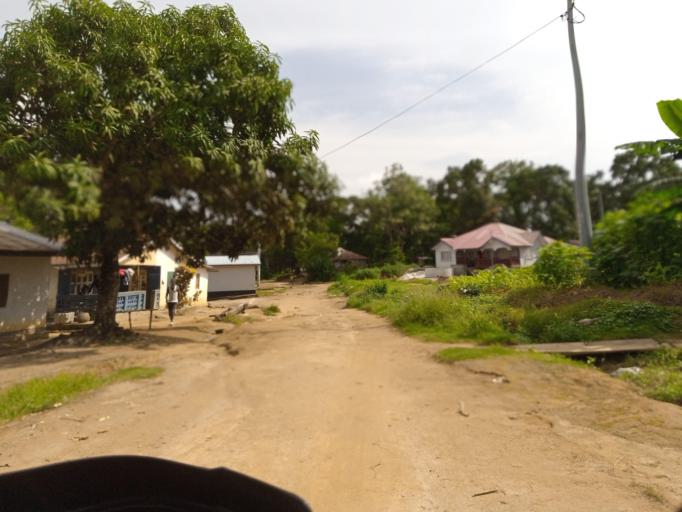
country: SL
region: Northern Province
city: Masoyila
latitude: 8.6062
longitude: -13.2046
